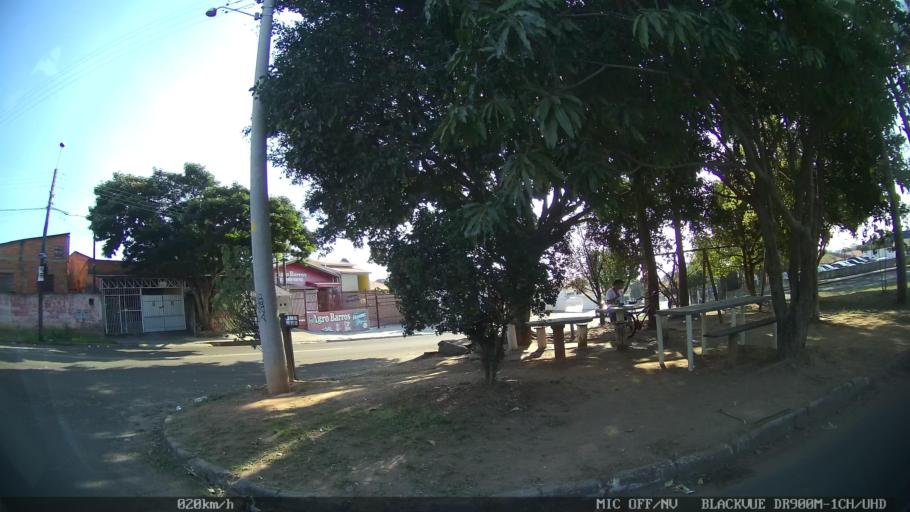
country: BR
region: Sao Paulo
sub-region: Indaiatuba
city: Indaiatuba
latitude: -22.9893
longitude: -47.1496
